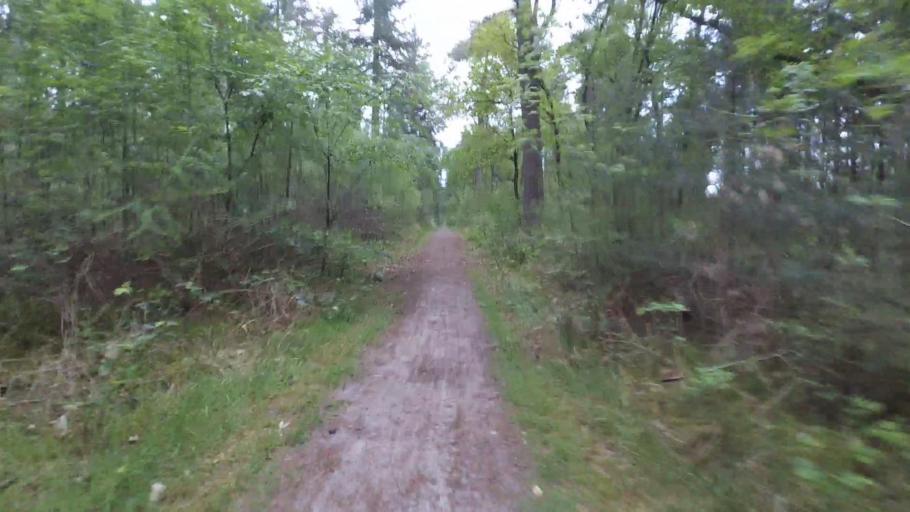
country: NL
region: Utrecht
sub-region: Gemeente Utrechtse Heuvelrug
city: Maarn
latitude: 52.0899
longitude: 5.3489
